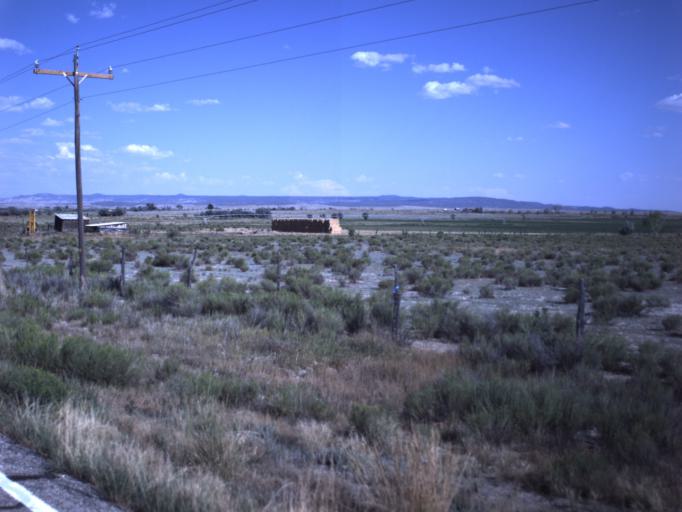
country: US
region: Utah
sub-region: Emery County
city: Huntington
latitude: 39.3450
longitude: -110.9005
